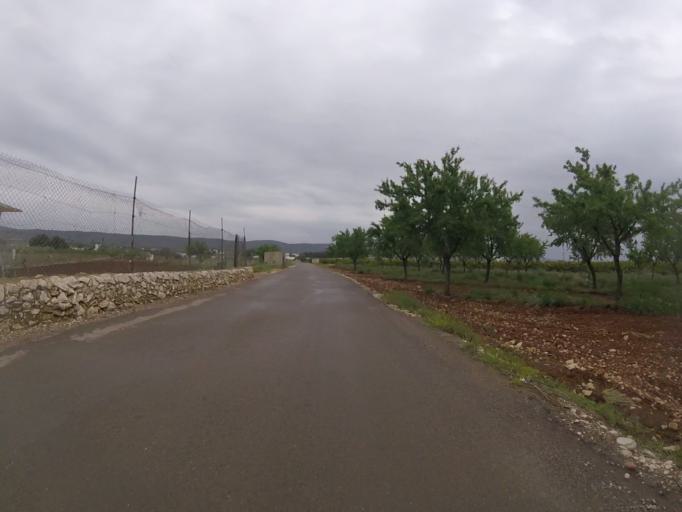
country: ES
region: Valencia
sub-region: Provincia de Castello
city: Alcala de Xivert
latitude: 40.2935
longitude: 0.2293
